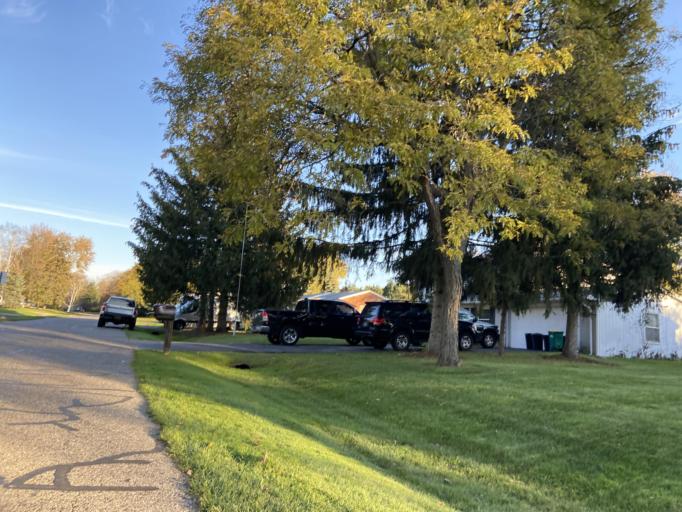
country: US
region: Michigan
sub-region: Oakland County
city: Farmington Hills
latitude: 42.5011
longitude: -83.3677
